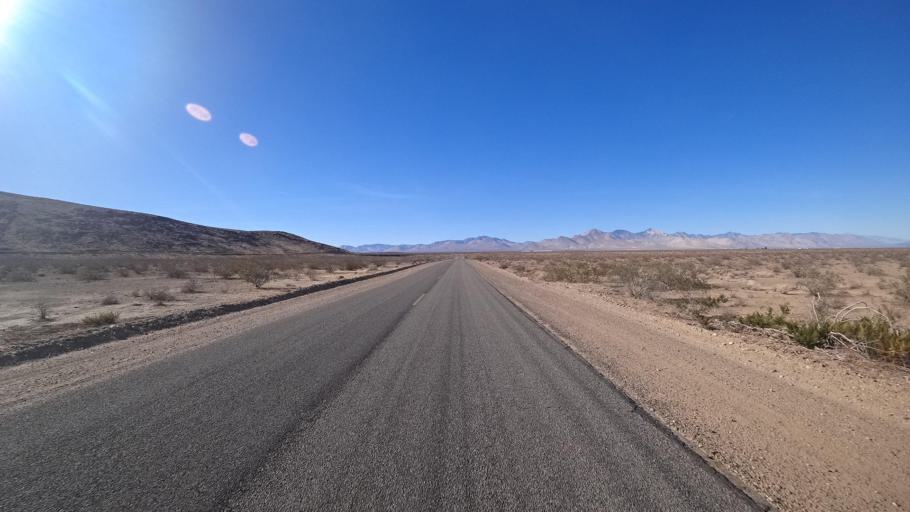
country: US
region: California
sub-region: Kern County
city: China Lake Acres
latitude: 35.5592
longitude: -117.7670
